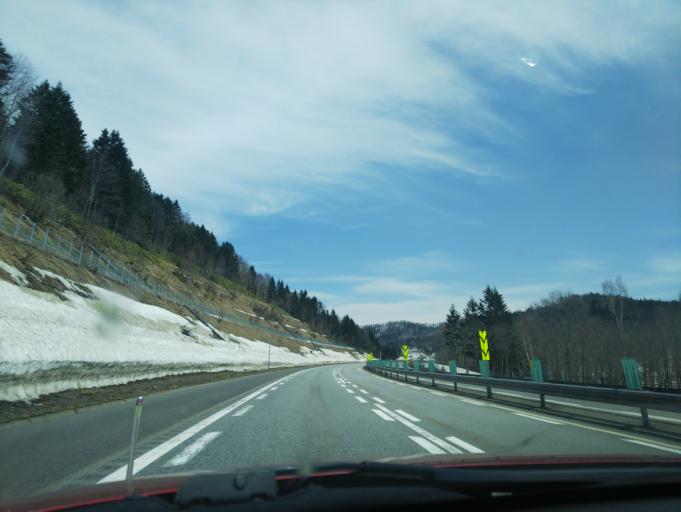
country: JP
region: Hokkaido
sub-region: Asahikawa-shi
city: Asahikawa
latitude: 43.7805
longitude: 142.1986
